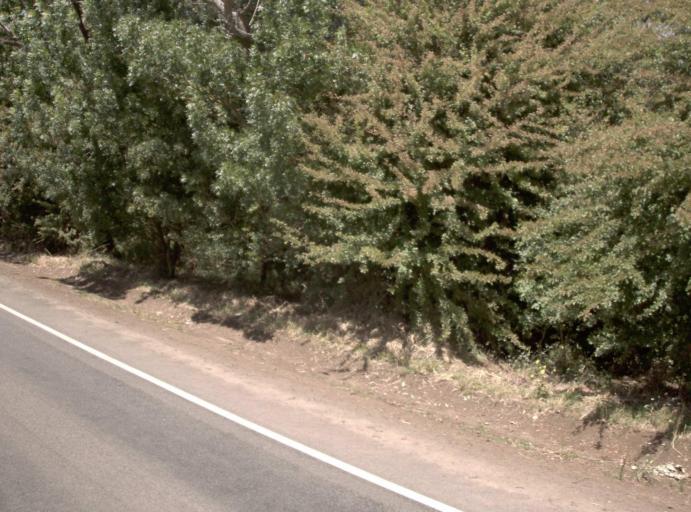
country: AU
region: Victoria
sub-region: Baw Baw
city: Warragul
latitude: -37.9729
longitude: 145.9500
